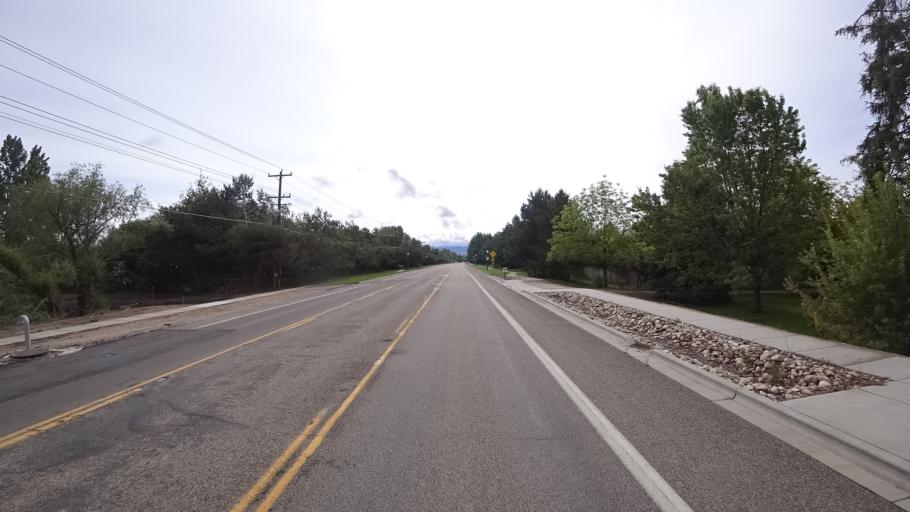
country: US
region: Idaho
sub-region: Ada County
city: Eagle
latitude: 43.6956
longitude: -116.3747
